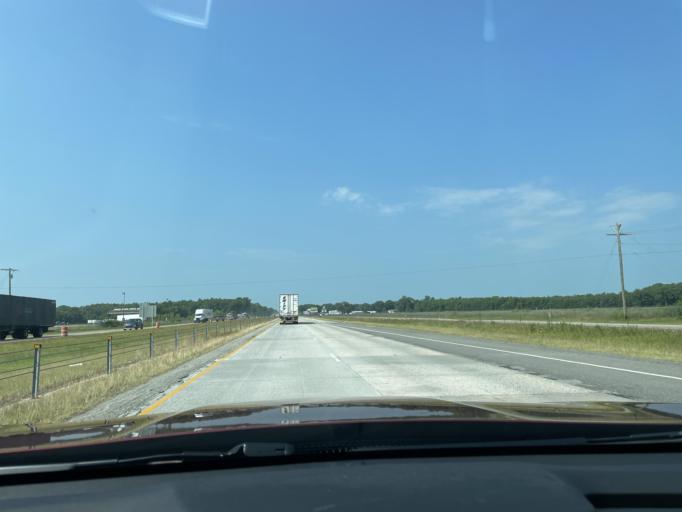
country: US
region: Arkansas
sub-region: White County
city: Searcy
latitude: 35.2001
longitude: -91.7369
